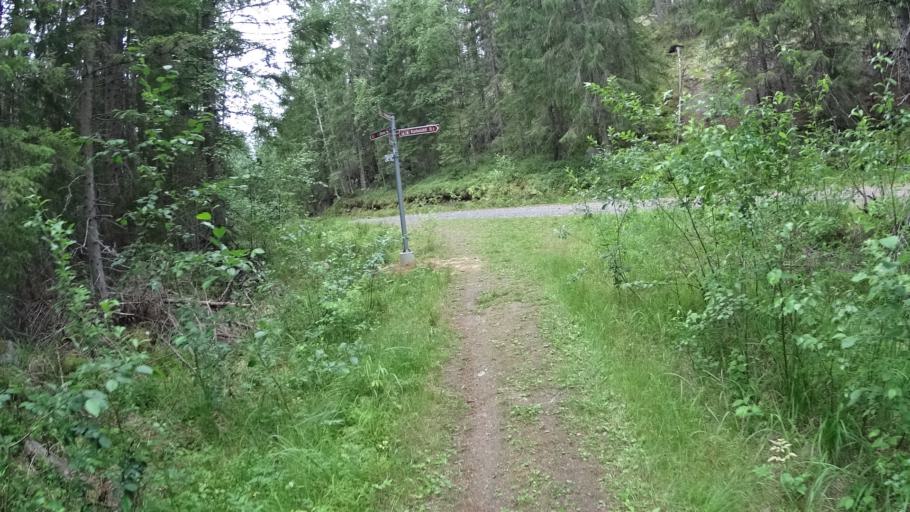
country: FI
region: Southern Savonia
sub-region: Mikkeli
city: Maentyharju
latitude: 61.1839
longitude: 26.8300
